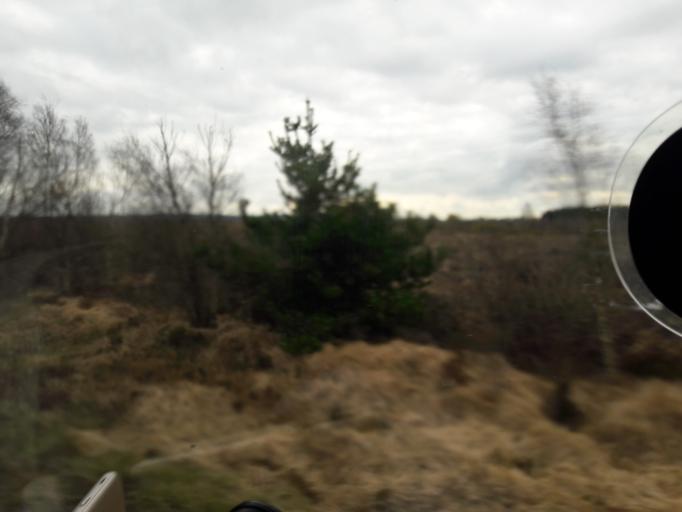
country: IE
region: Leinster
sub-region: An Longfort
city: Granard
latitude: 53.6643
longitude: -7.4692
